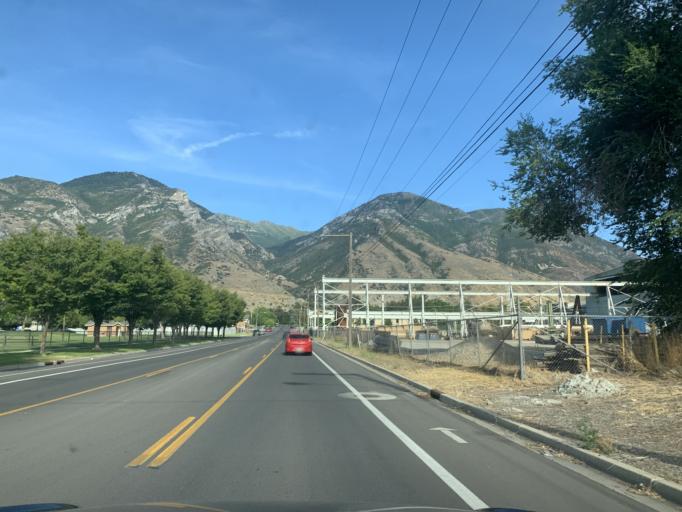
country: US
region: Utah
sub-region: Utah County
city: Provo
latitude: 40.2256
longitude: -111.6516
